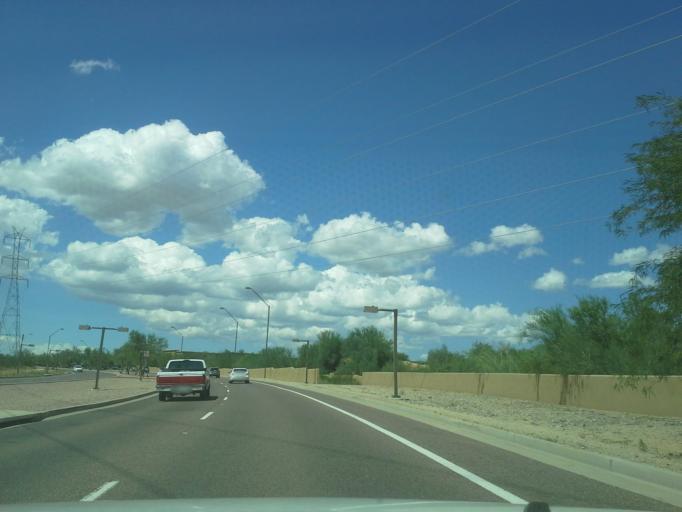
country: US
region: Arizona
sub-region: Maricopa County
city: Paradise Valley
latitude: 33.6672
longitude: -111.9043
